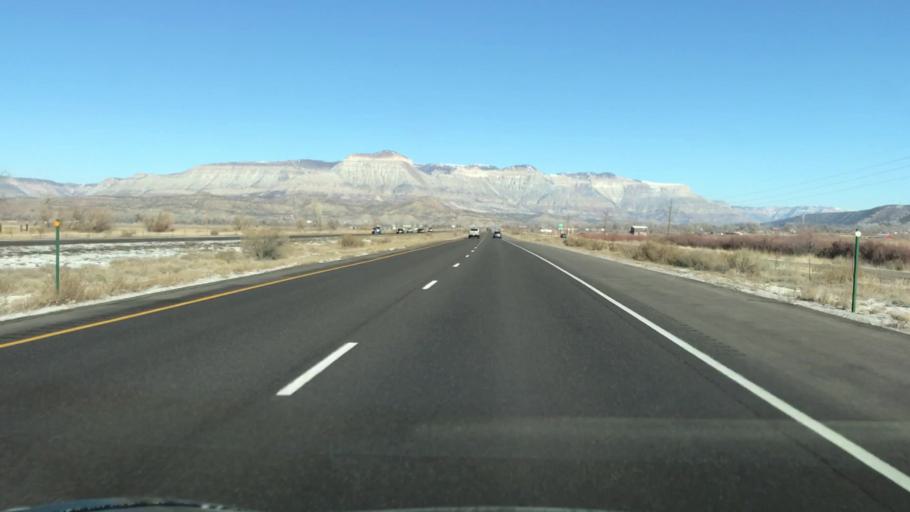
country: US
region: Colorado
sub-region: Mesa County
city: Palisade
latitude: 39.2945
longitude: -108.2222
